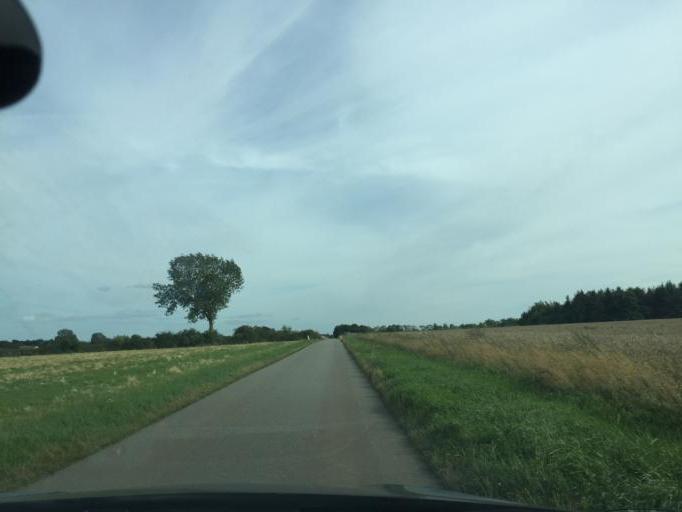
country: DK
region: South Denmark
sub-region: Kerteminde Kommune
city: Langeskov
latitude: 55.3362
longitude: 10.5526
